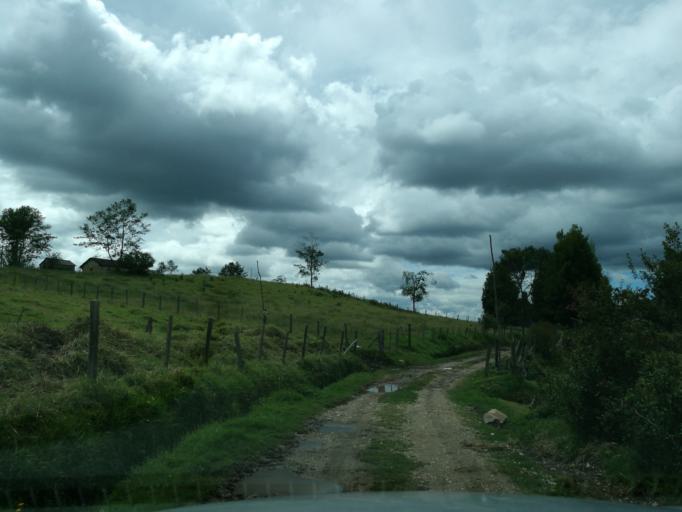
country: CO
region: Boyaca
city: Arcabuco
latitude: 5.7490
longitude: -73.4637
